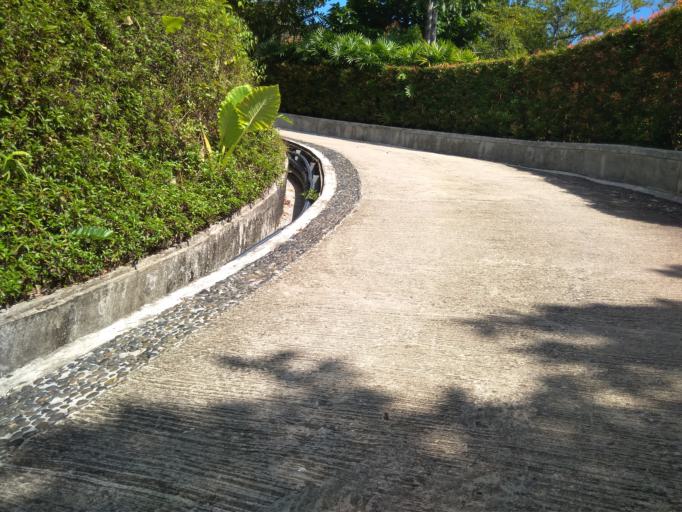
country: TH
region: Krabi
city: Ko Lanta
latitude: 7.4953
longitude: 99.0773
